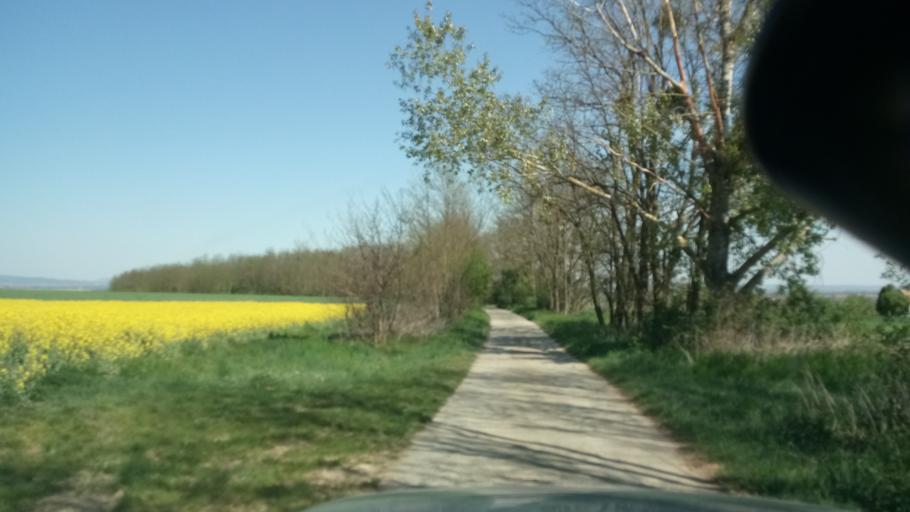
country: HU
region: Zala
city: Sarmellek
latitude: 46.7032
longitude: 17.0940
